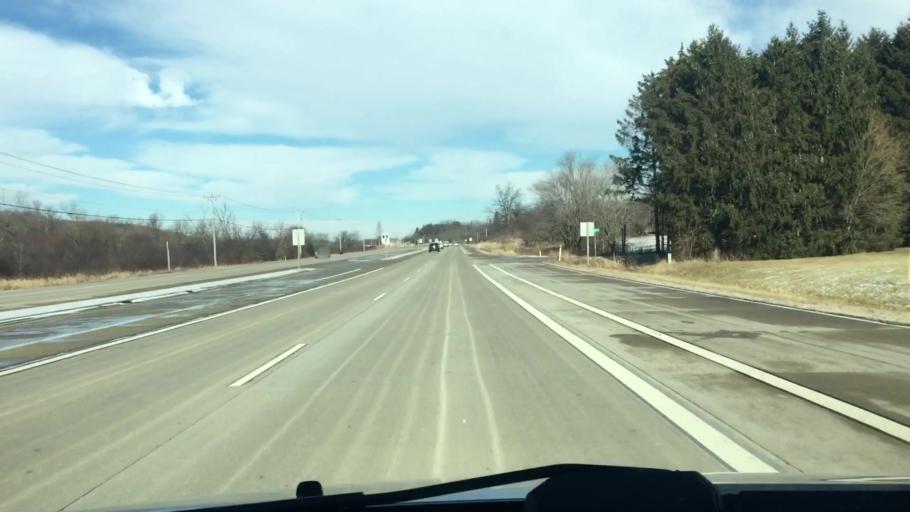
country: US
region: Wisconsin
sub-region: Waukesha County
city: Mukwonago
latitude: 42.8916
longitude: -88.3436
